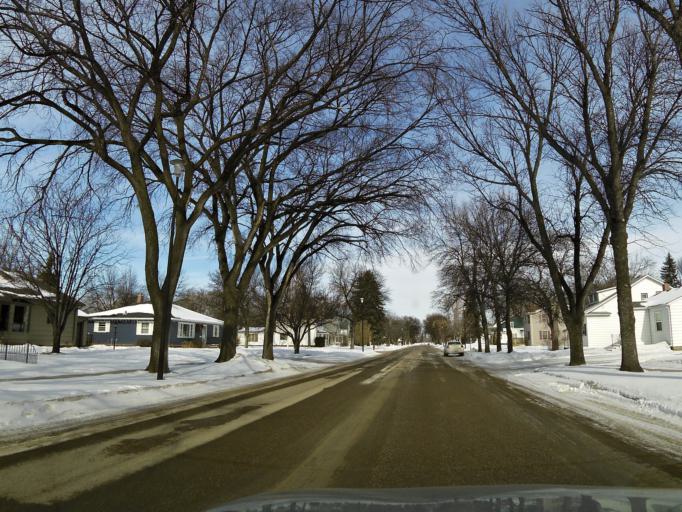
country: US
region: North Dakota
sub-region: Walsh County
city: Grafton
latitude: 48.4149
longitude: -97.4173
